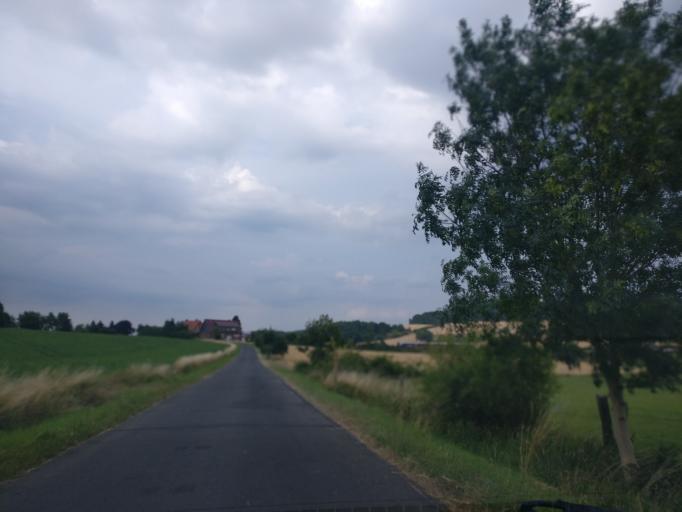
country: DE
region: Lower Saxony
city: Adelebsen
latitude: 51.5906
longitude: 9.7800
